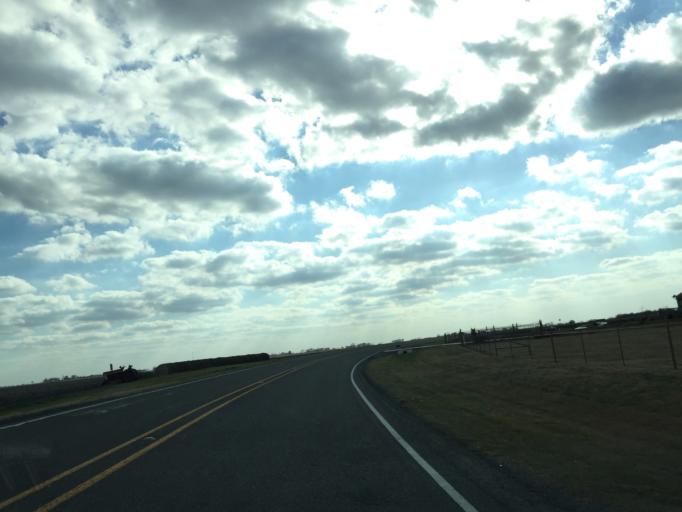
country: US
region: Texas
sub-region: Williamson County
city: Taylor
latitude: 30.6420
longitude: -97.4086
